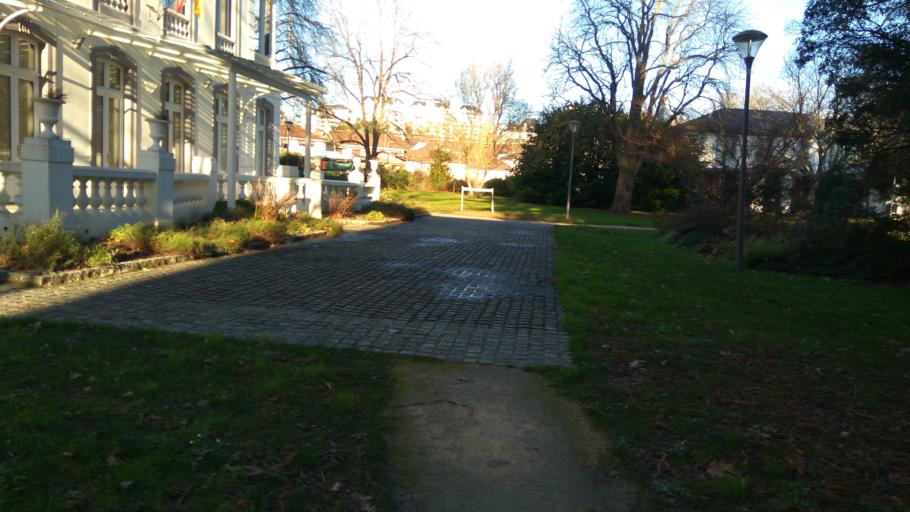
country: FR
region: Aquitaine
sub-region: Departement des Pyrenees-Atlantiques
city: Billere
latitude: 43.3018
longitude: -0.3979
